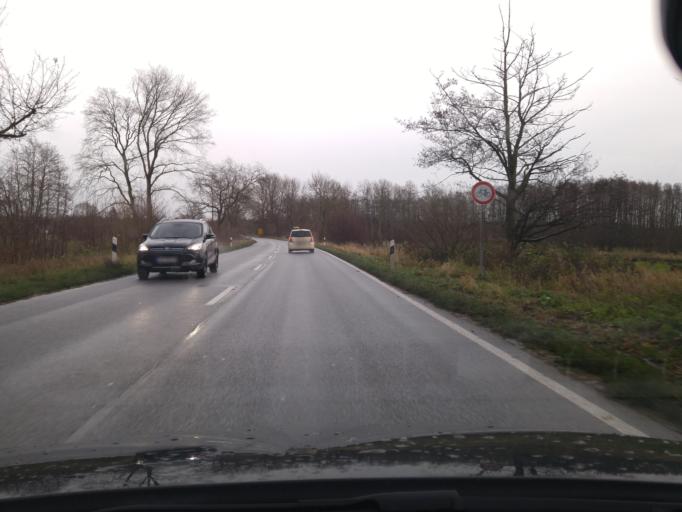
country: DE
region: Schleswig-Holstein
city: Timmendorfer Strand
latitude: 53.9909
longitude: 10.7832
